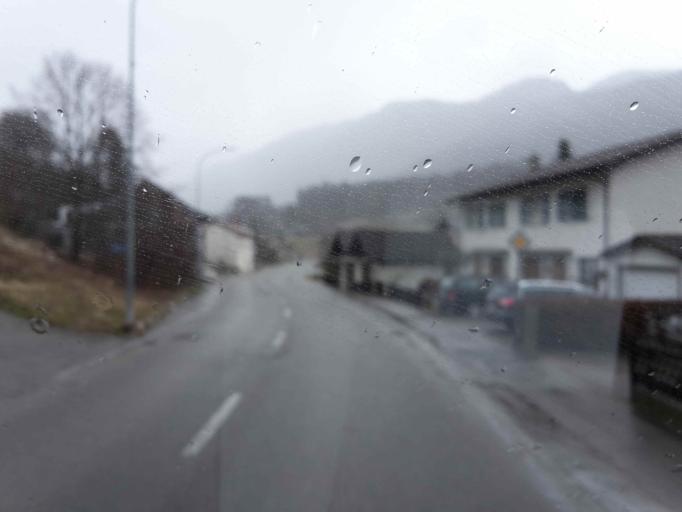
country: CH
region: Solothurn
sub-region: Bezirk Thal
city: Welschenrohr
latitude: 47.2806
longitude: 7.5320
